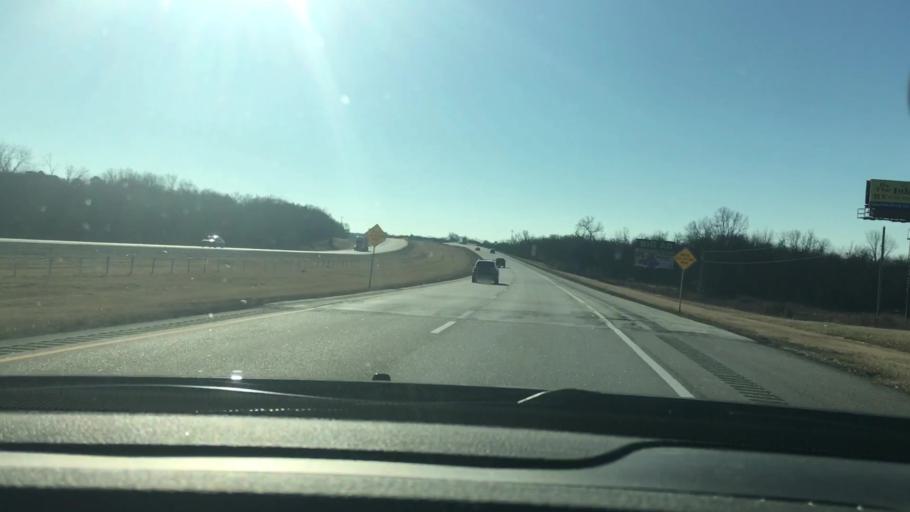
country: US
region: Oklahoma
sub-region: Carter County
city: Ardmore
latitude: 34.1639
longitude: -97.1666
